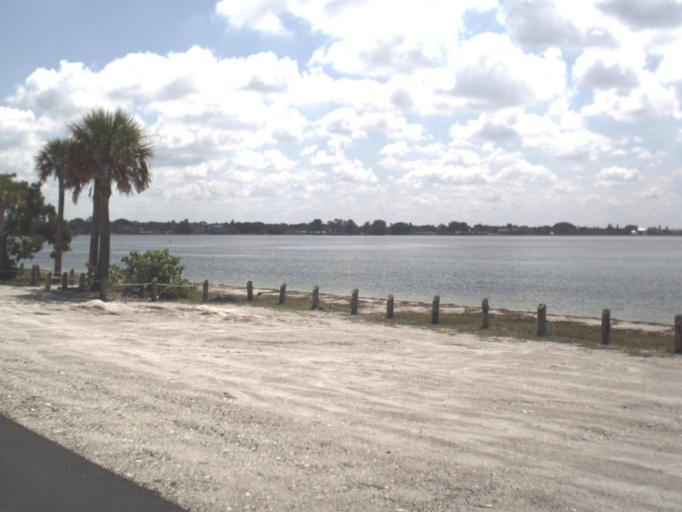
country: US
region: Florida
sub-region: Manatee County
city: Cortez
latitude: 27.4962
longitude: -82.6568
